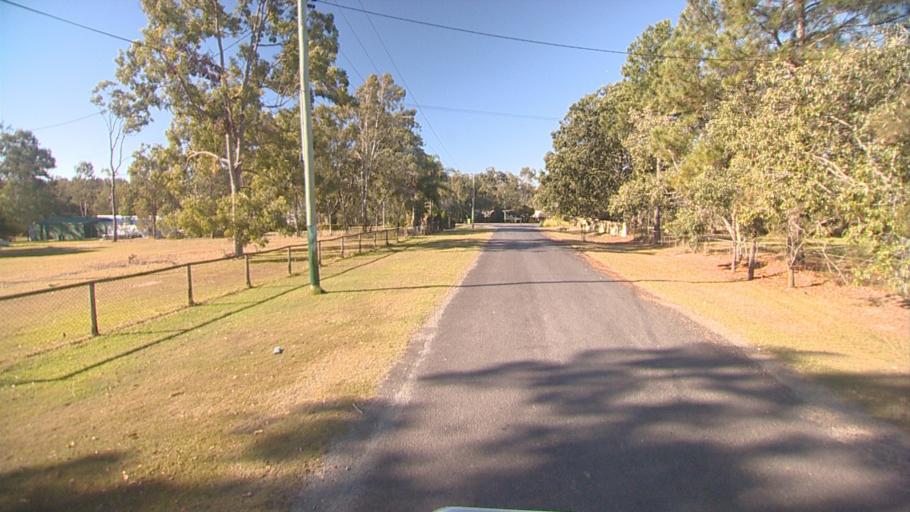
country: AU
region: Queensland
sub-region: Logan
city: Park Ridge South
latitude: -27.7313
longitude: 153.0257
